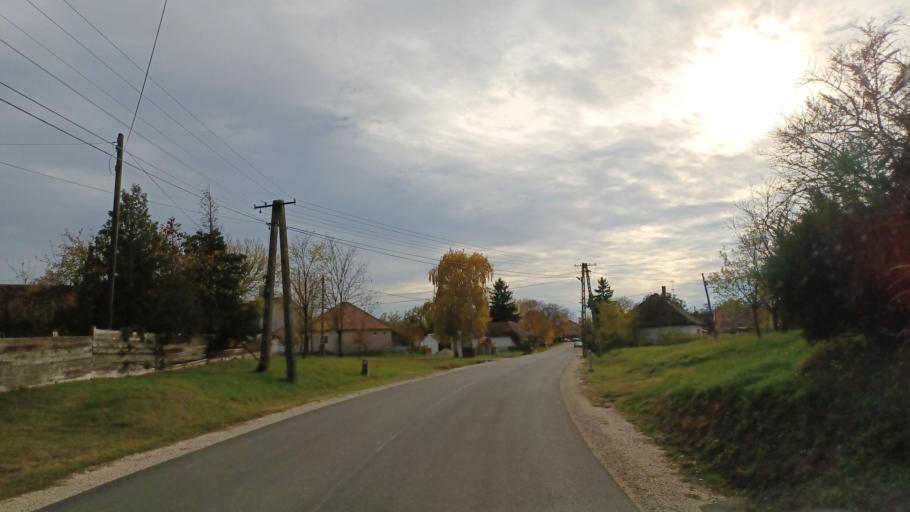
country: HU
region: Fejer
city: Cece
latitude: 46.7171
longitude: 18.6194
